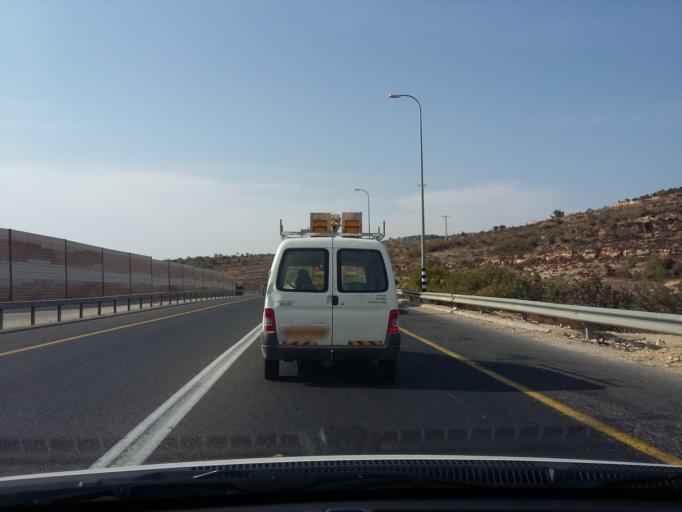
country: PS
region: West Bank
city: Al Khadir
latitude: 31.6985
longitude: 35.1559
